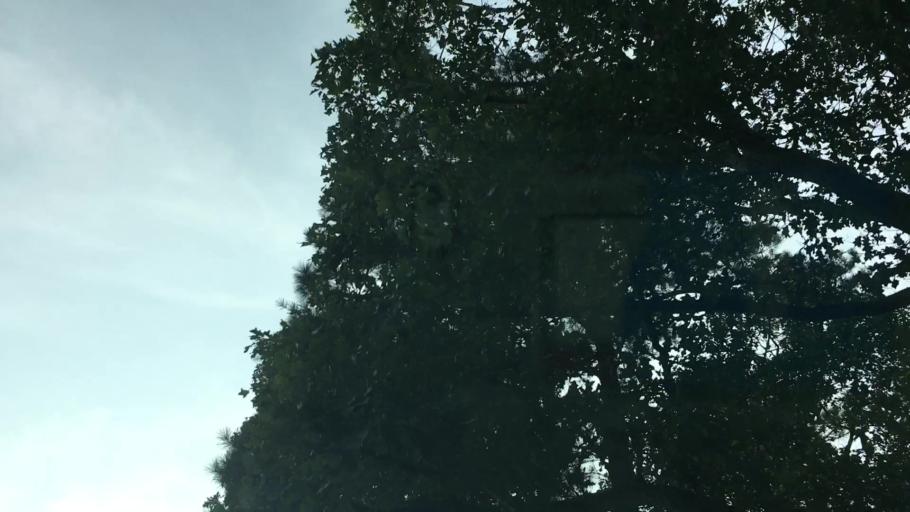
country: US
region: Alabama
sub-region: Bibb County
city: Woodstock
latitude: 33.2183
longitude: -87.1141
